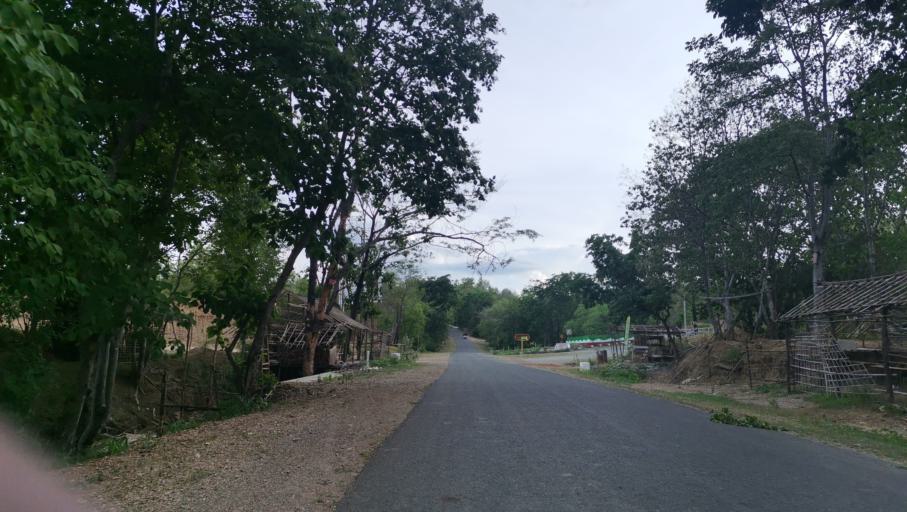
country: MM
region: Magway
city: Minbu
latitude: 20.0868
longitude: 94.5789
